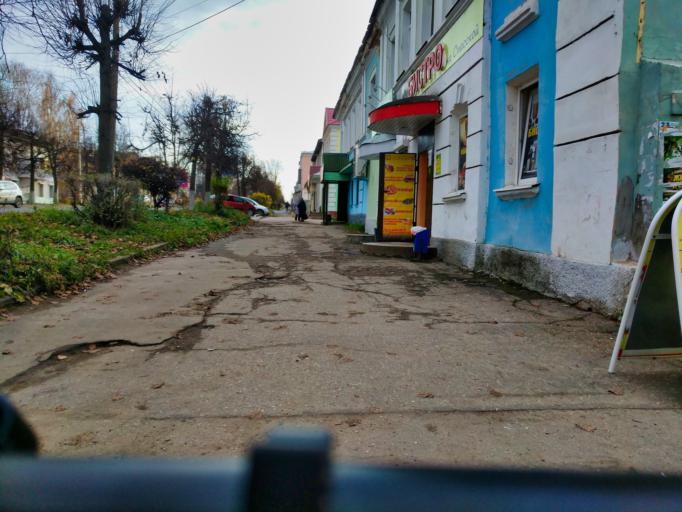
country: RU
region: Tverskaya
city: Rzhev
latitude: 56.2563
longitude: 34.3279
